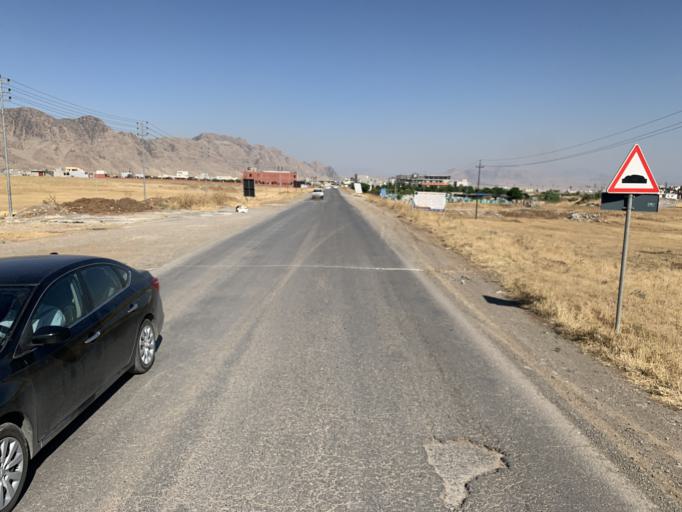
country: IQ
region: As Sulaymaniyah
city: Raniye
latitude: 36.2625
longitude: 44.8511
